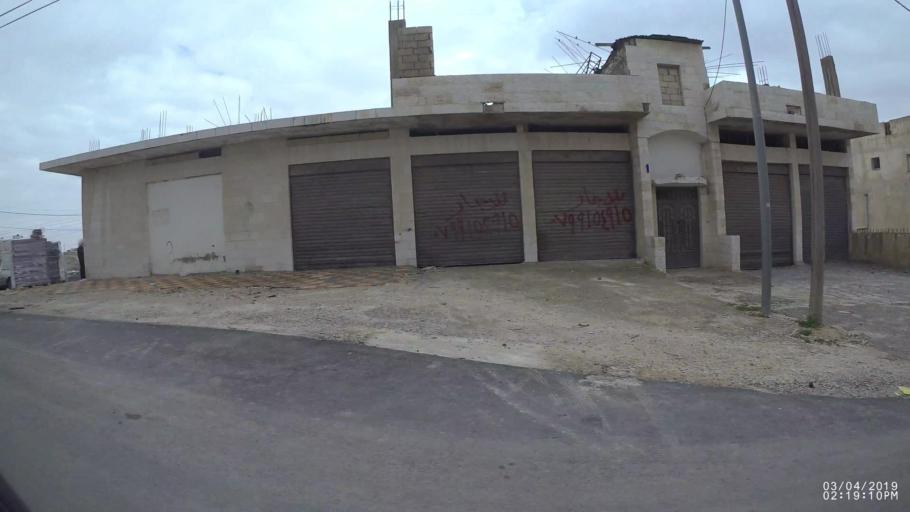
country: JO
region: Amman
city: Wadi as Sir
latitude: 31.9395
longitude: 35.8342
